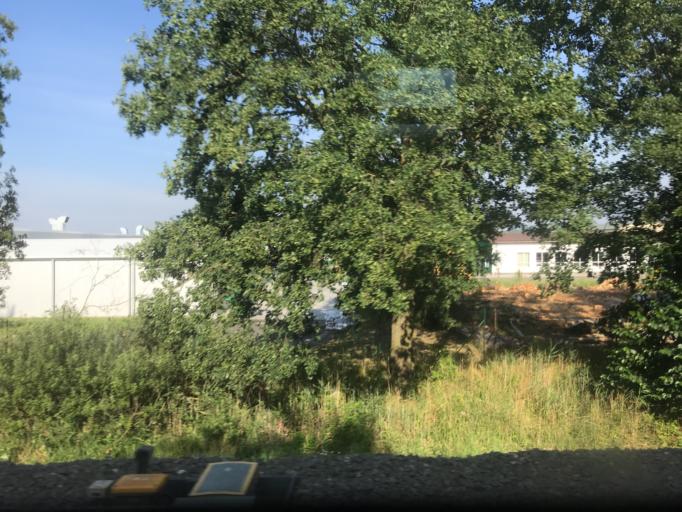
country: CZ
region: Jihocesky
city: Sobeslav
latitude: 49.2464
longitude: 14.7248
